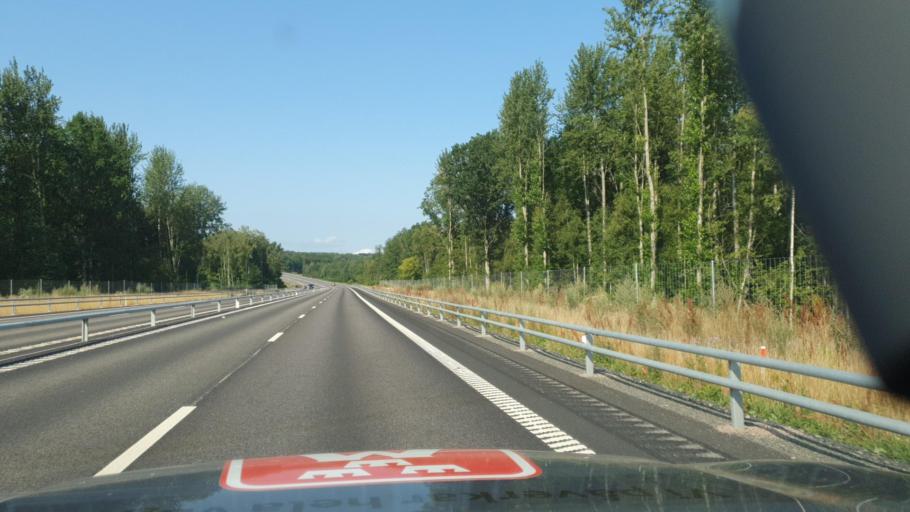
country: SE
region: Skane
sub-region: Kristianstads Kommun
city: Onnestad
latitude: 55.9513
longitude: 13.9100
